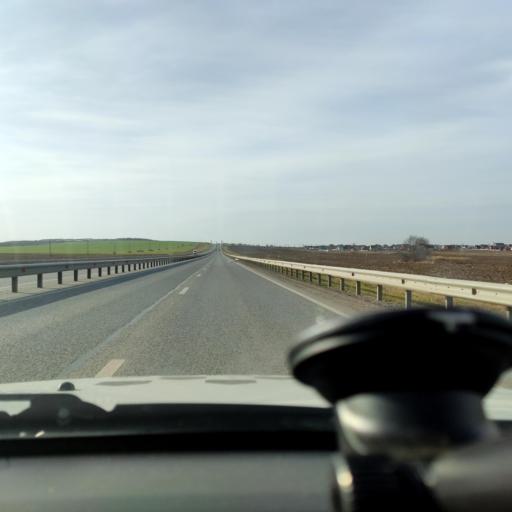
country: RU
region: Perm
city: Kultayevo
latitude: 57.8796
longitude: 55.9107
